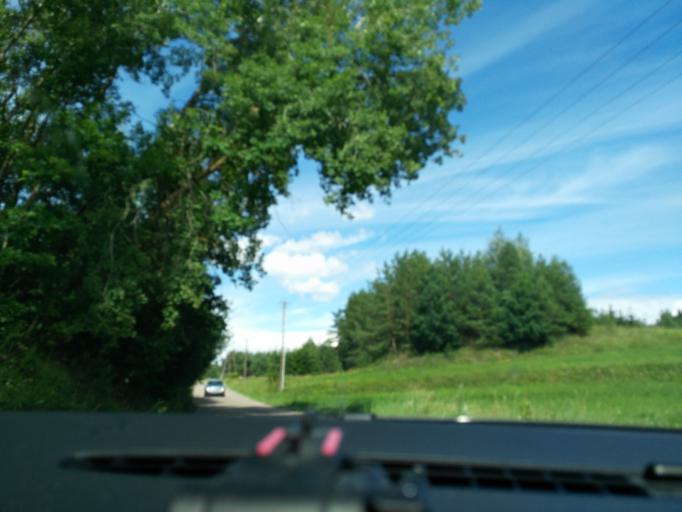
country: PL
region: Podlasie
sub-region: Powiat sejnenski
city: Sejny
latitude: 54.0330
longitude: 23.3209
